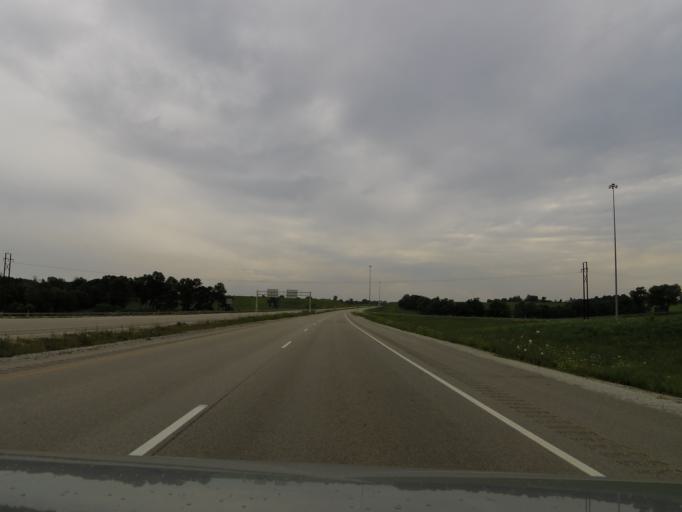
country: US
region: Ohio
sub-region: Brown County
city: Aberdeen
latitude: 38.6401
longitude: -83.8323
